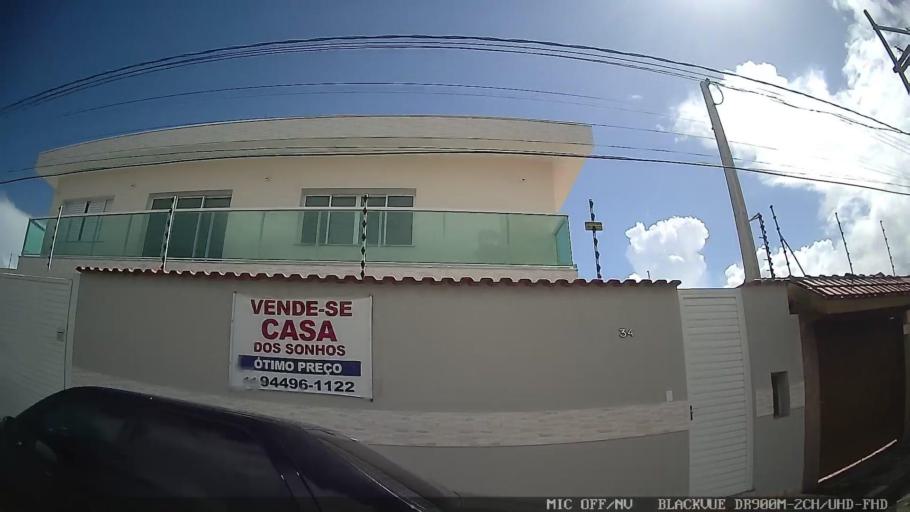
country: BR
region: Sao Paulo
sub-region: Itanhaem
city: Itanhaem
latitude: -24.1963
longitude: -46.8029
